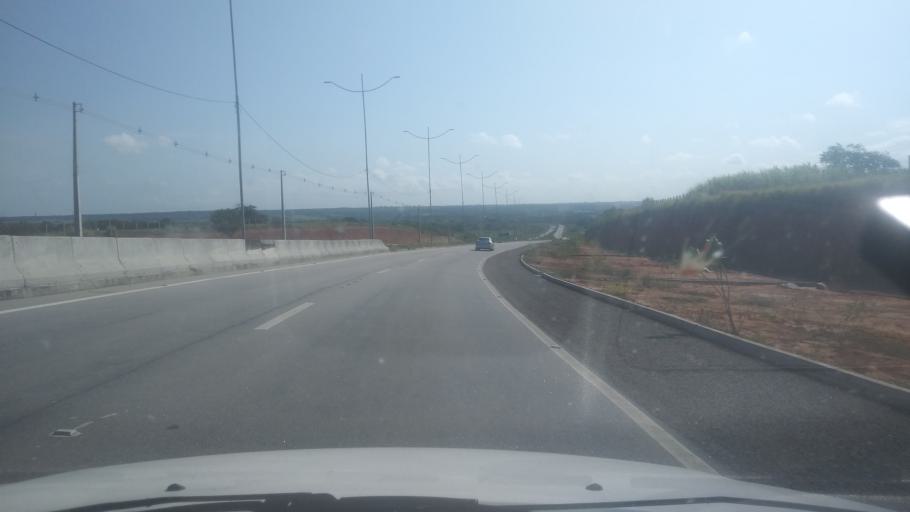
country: BR
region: Rio Grande do Norte
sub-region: Macaiba
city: Macaiba
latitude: -5.8245
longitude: -35.3695
